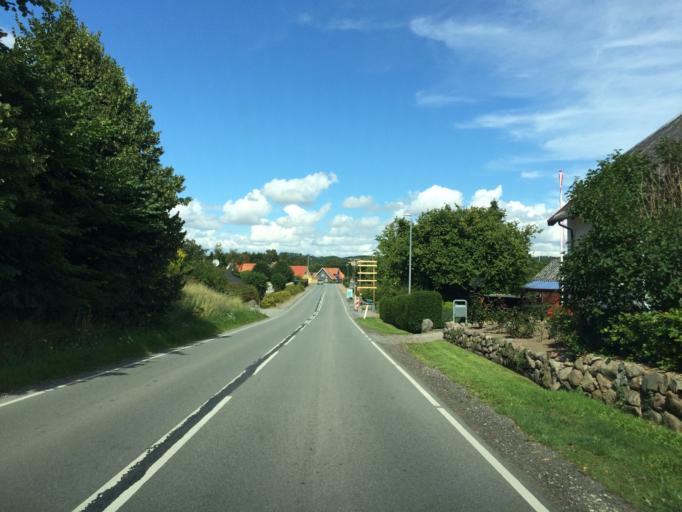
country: DK
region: South Denmark
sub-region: Faaborg-Midtfyn Kommune
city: Faaborg
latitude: 55.1284
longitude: 10.2123
